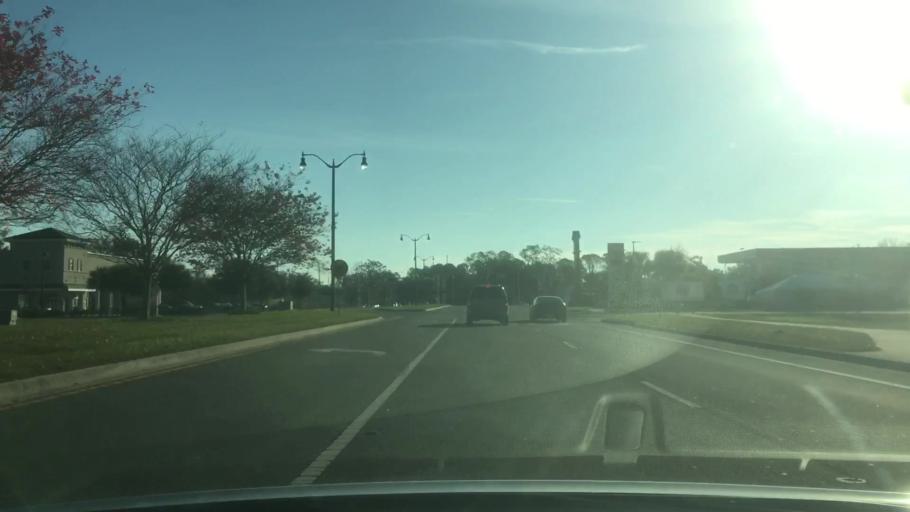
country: US
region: Florida
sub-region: Duval County
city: Jacksonville
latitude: 30.4761
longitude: -81.6321
